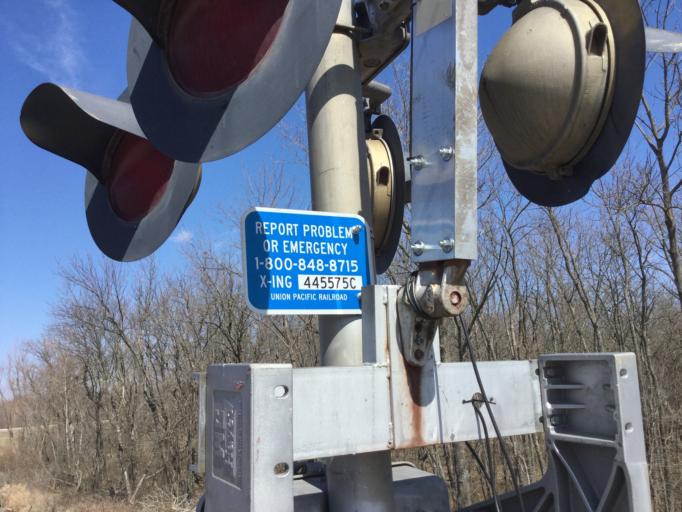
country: US
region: Kansas
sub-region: Wilson County
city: Fredonia
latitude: 37.6299
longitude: -95.7477
